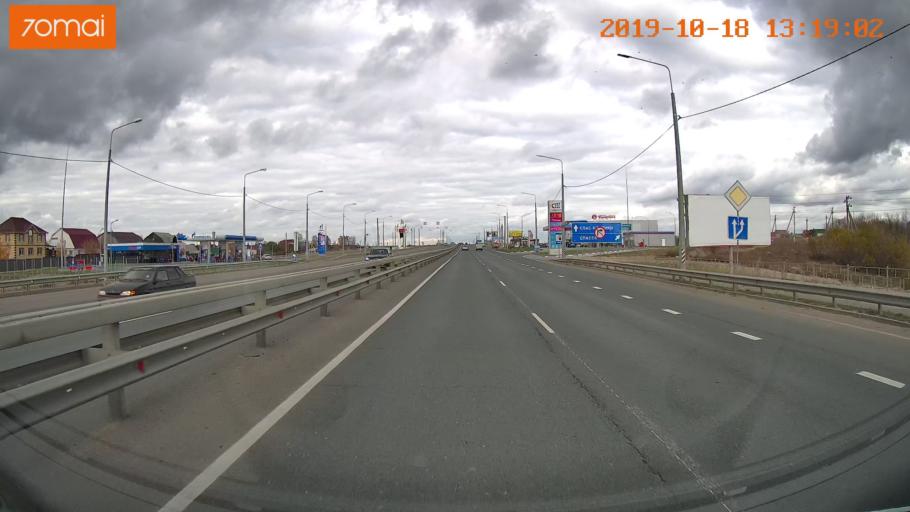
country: RU
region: Rjazan
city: Polyany
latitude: 54.6623
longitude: 39.8223
